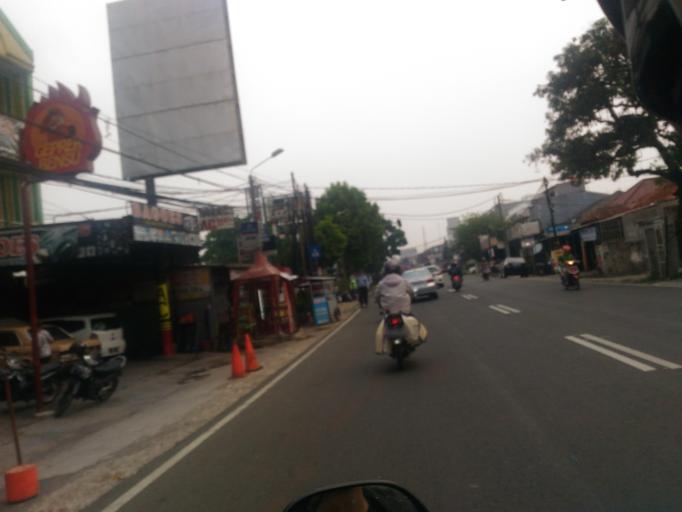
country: ID
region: West Java
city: Bogor
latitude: -6.6311
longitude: 106.8247
